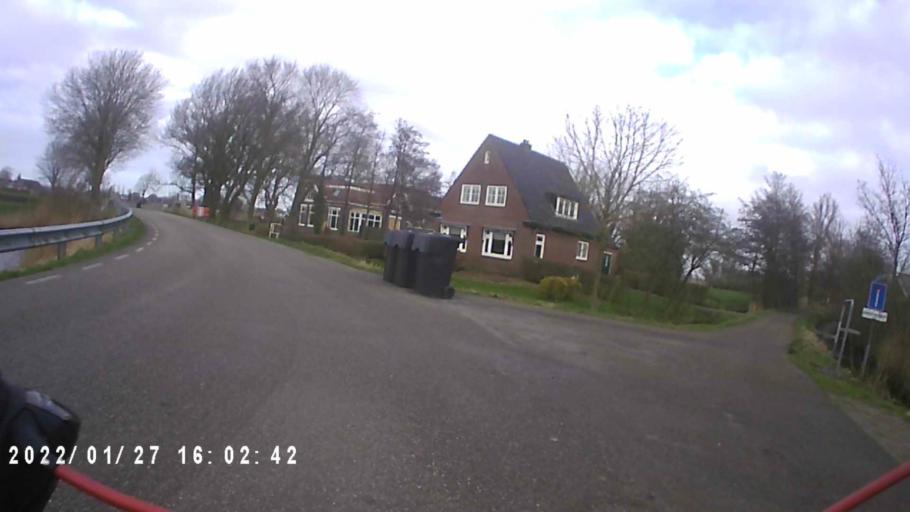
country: NL
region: Friesland
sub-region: Gemeente Dongeradeel
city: Anjum
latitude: 53.3757
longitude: 6.0897
